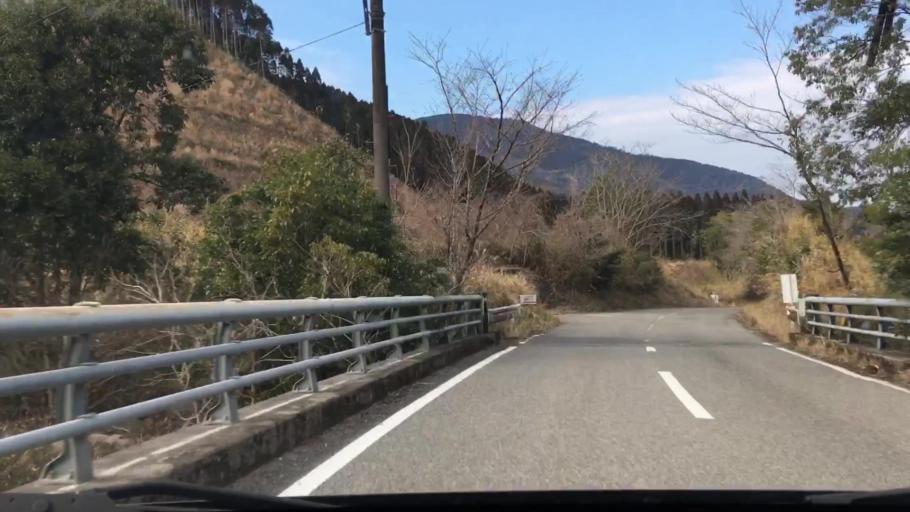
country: JP
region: Miyazaki
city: Nichinan
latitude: 31.7082
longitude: 131.3266
